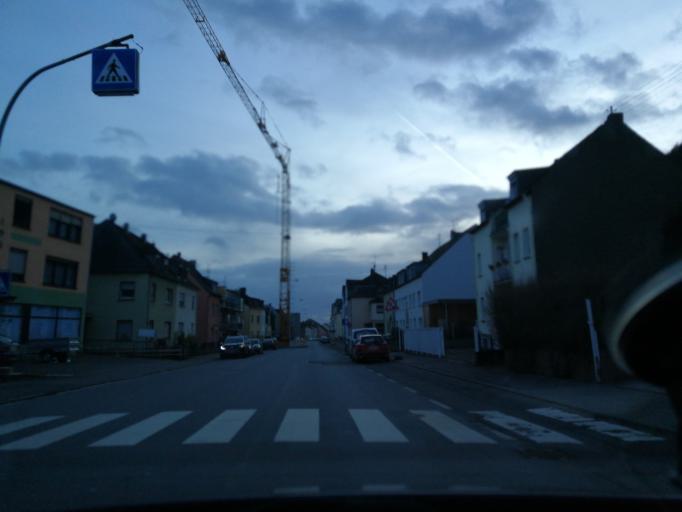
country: DE
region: Rheinland-Pfalz
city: Trier
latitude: 49.7833
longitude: 6.6707
